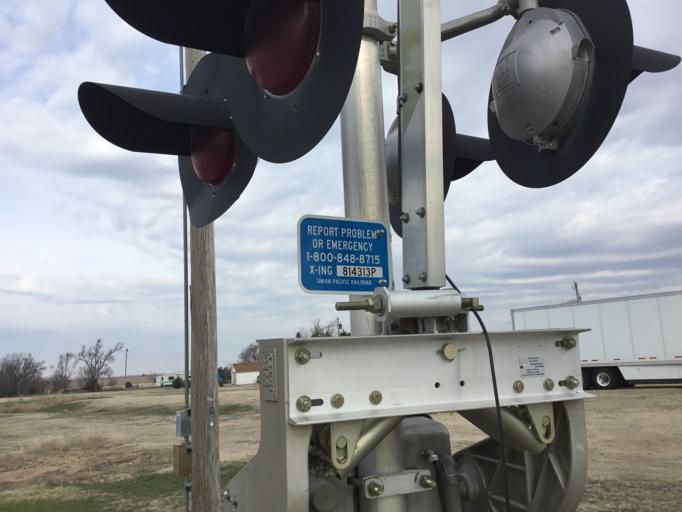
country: US
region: Kansas
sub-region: Ellis County
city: Victoria
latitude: 38.8810
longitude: -99.0236
